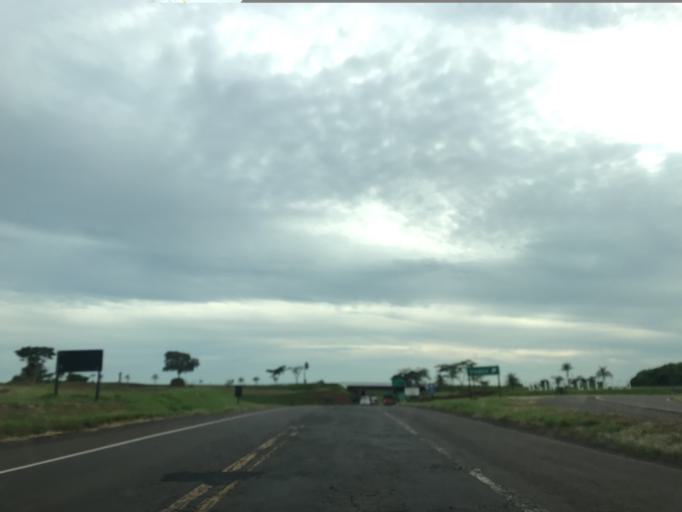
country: BR
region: Sao Paulo
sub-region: Birigui
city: Birigui
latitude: -21.5701
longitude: -50.4405
